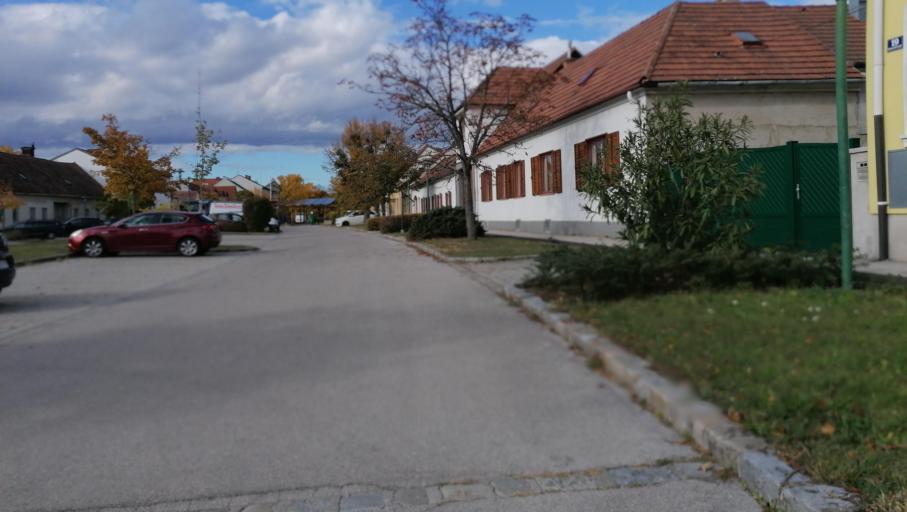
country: AT
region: Lower Austria
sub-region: Politischer Bezirk Baden
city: Tattendorf
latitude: 47.9548
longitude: 16.3041
